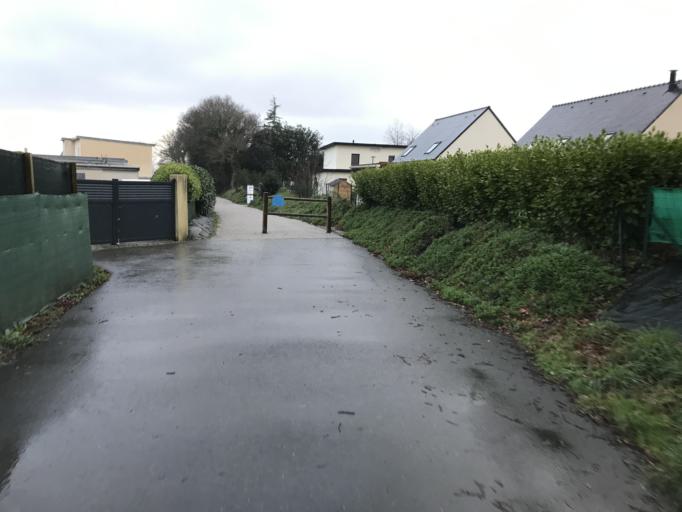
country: FR
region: Brittany
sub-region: Departement du Finistere
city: Loperhet
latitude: 48.3726
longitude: -4.3176
